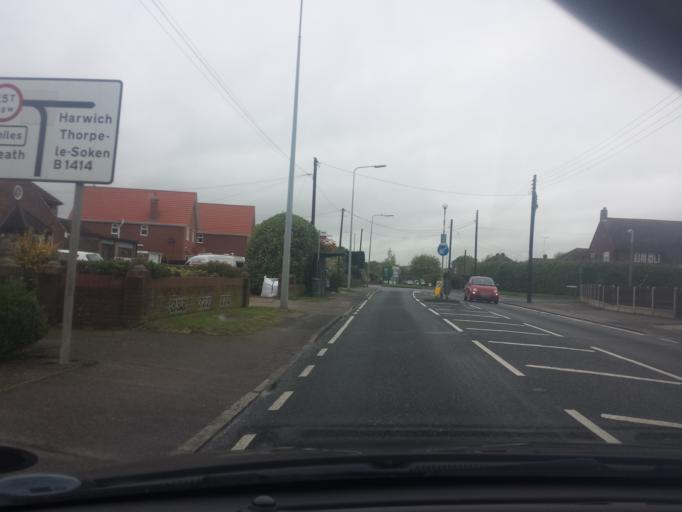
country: GB
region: England
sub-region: Essex
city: Little Clacton
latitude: 51.8345
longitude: 1.1389
